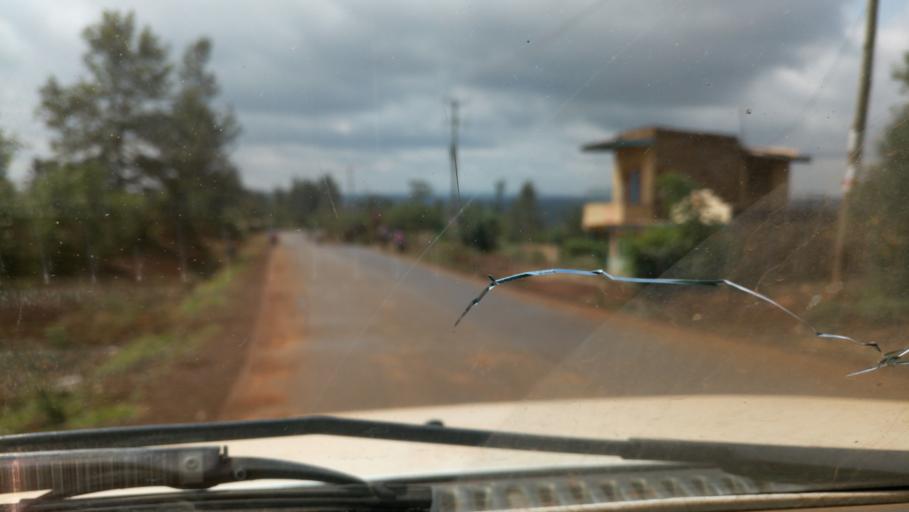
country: KE
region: Murang'a District
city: Maragua
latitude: -0.8801
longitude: 37.1280
